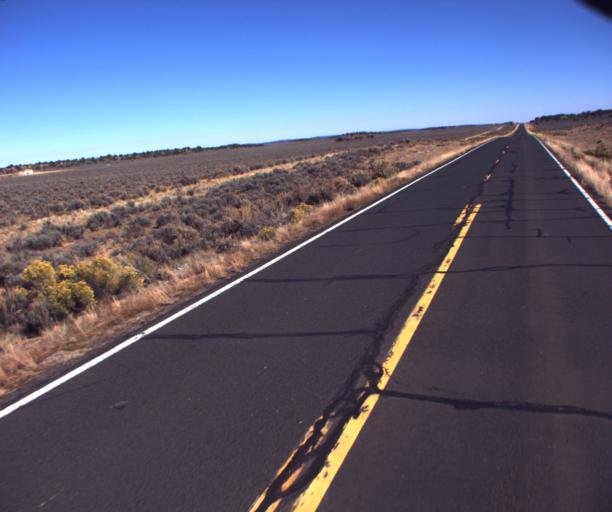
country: US
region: Arizona
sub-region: Navajo County
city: First Mesa
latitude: 35.7422
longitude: -110.0691
